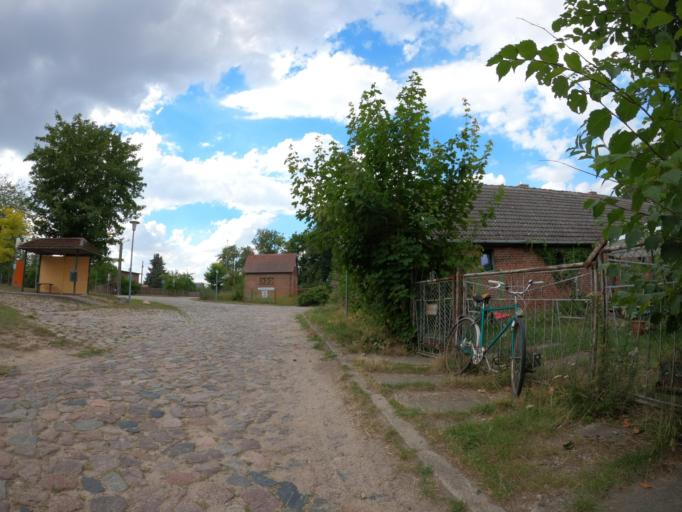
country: DE
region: Mecklenburg-Vorpommern
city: Woldegk
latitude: 53.4152
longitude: 13.6154
